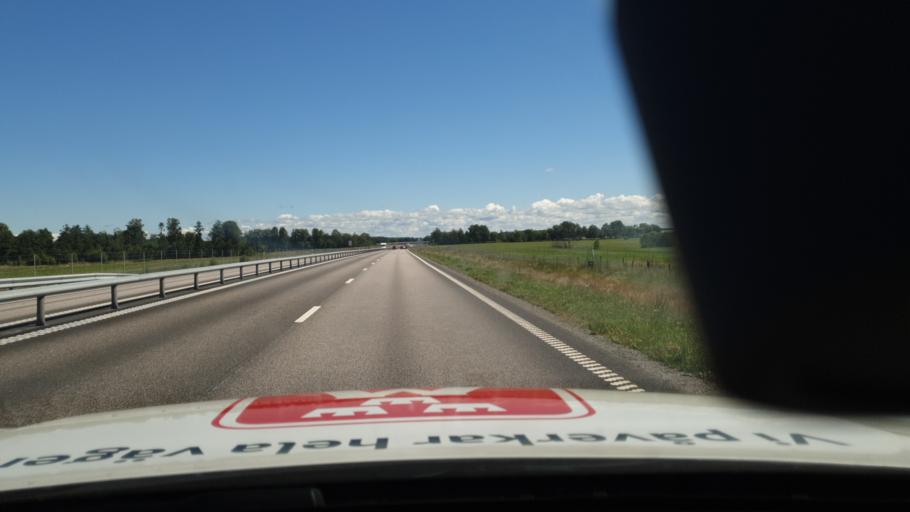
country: SE
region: Vaestra Goetaland
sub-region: Lidkopings Kommun
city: Vinninga
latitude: 58.4793
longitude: 13.2170
